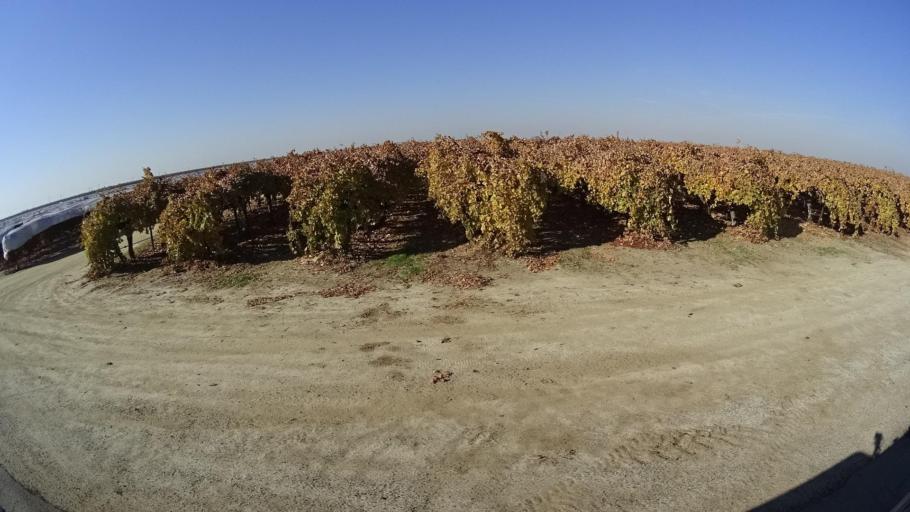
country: US
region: California
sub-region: Kern County
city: McFarland
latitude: 35.7218
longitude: -119.2051
